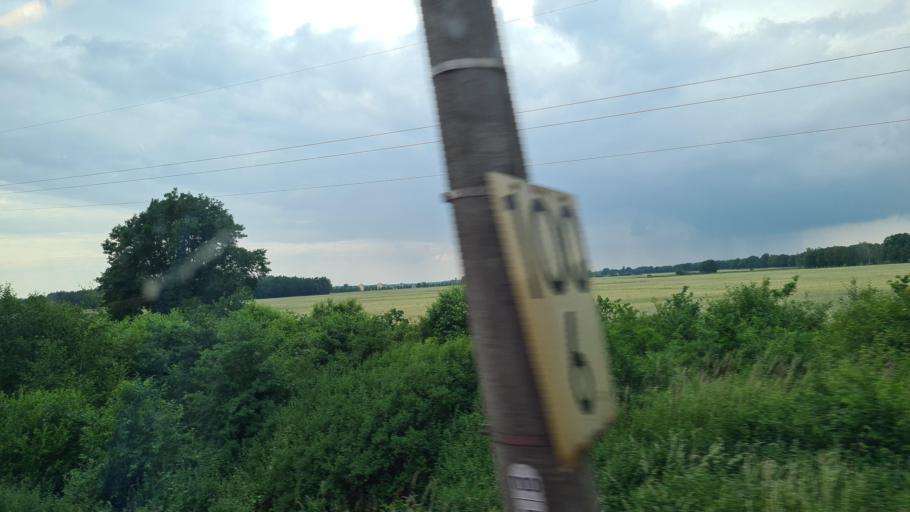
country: DE
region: Brandenburg
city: Schilda
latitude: 51.5878
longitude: 13.3270
